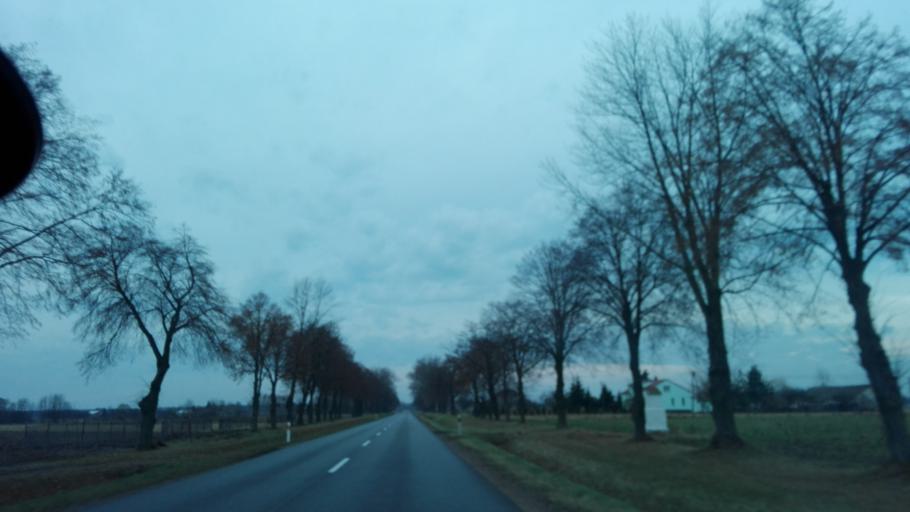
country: PL
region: Lublin Voivodeship
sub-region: Powiat radzynski
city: Wohyn
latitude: 51.7794
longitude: 22.7763
